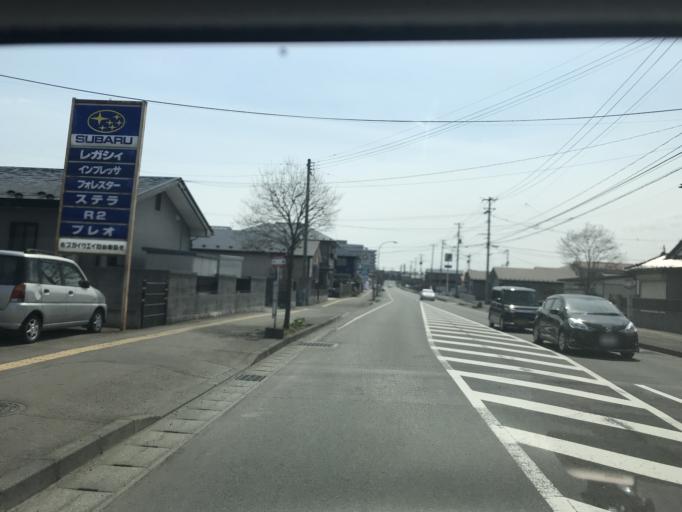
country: JP
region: Iwate
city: Mizusawa
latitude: 39.1284
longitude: 141.1357
